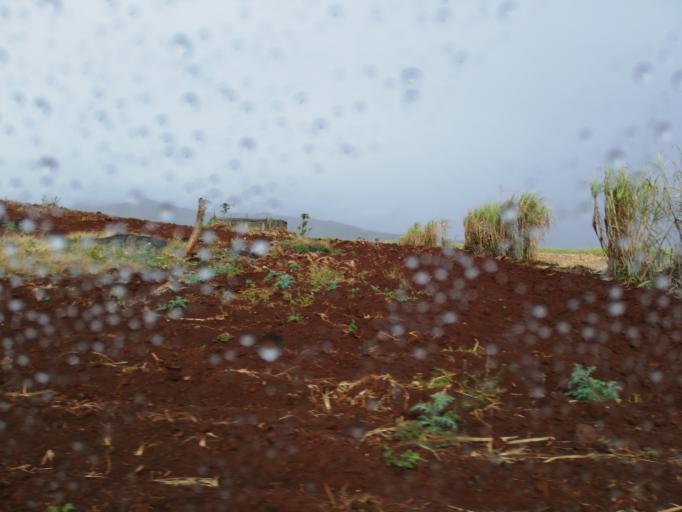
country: MU
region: Pamplemousses
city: Long Mountain
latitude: -20.1272
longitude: 57.5659
